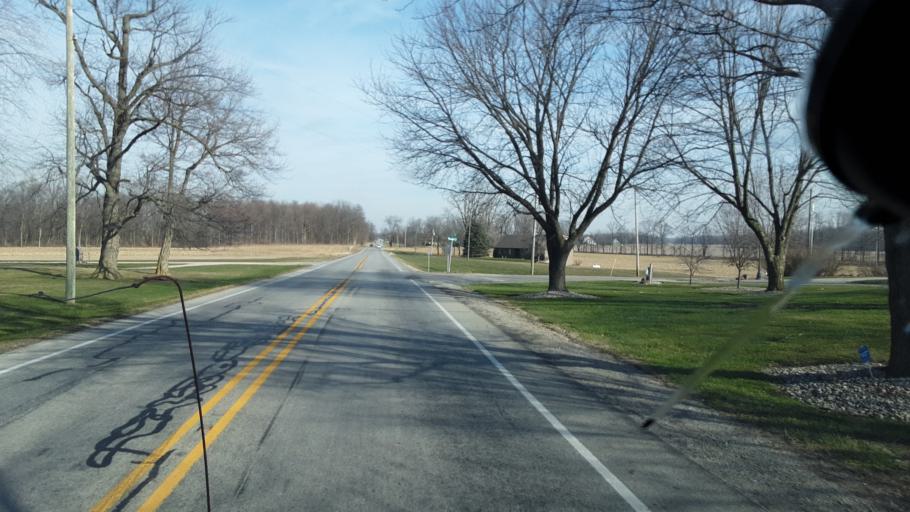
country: US
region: Indiana
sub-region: Allen County
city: Harlan
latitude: 41.2106
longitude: -84.8993
